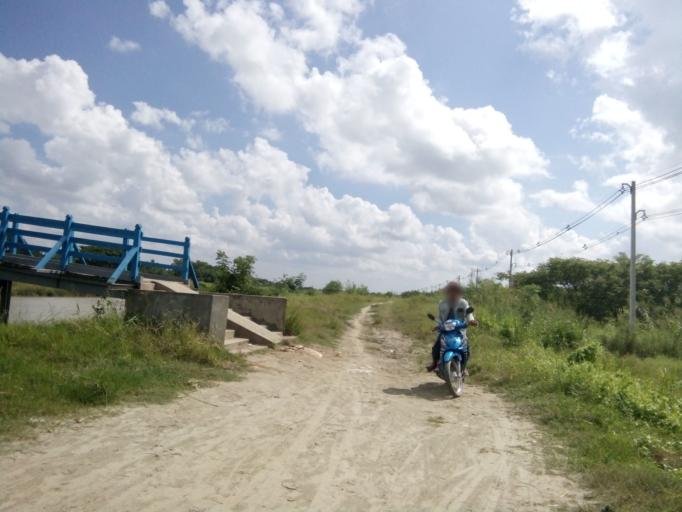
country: MM
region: Yangon
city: Kanbe
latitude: 16.8708
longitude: 95.9811
